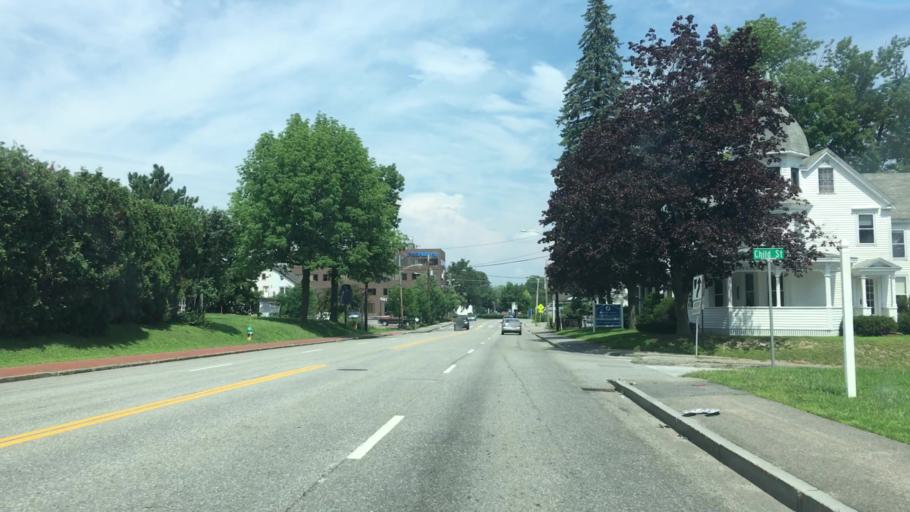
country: US
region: Maine
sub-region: Kennebec County
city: Augusta
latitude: 44.3080
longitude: -69.7806
